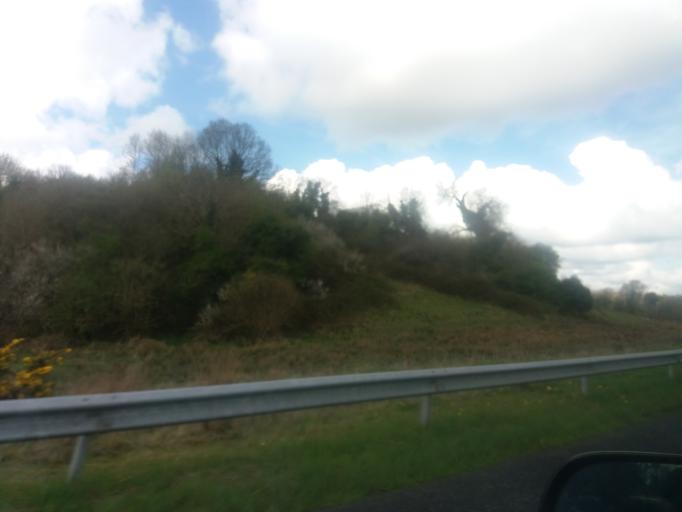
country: IE
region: Ulster
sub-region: An Cabhan
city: Belturbet
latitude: 54.0712
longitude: -7.4108
